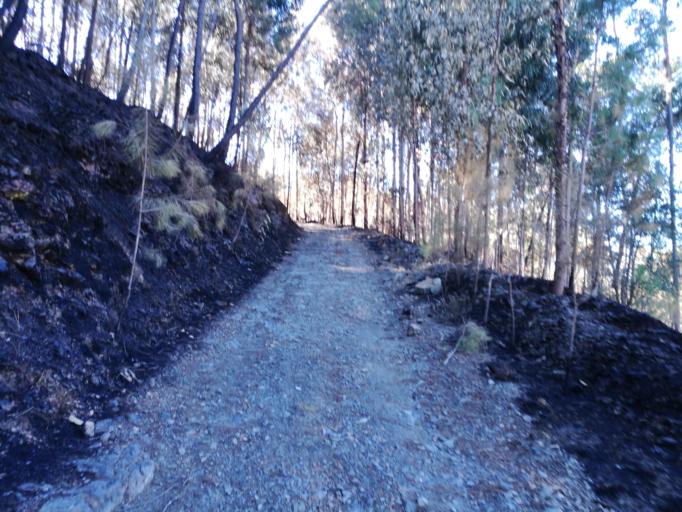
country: PT
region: Leiria
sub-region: Pedrogao Grande
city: Pedrogao Grande
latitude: 39.9151
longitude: -8.0637
